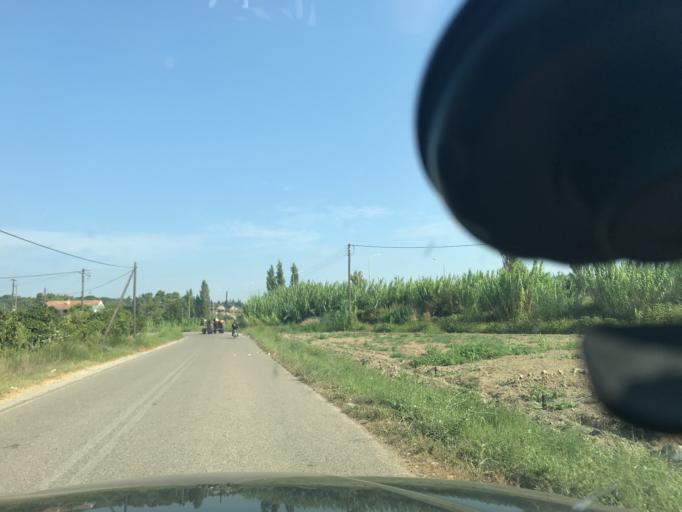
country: GR
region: West Greece
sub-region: Nomos Ileias
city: Kardamas
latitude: 37.7188
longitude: 21.3692
